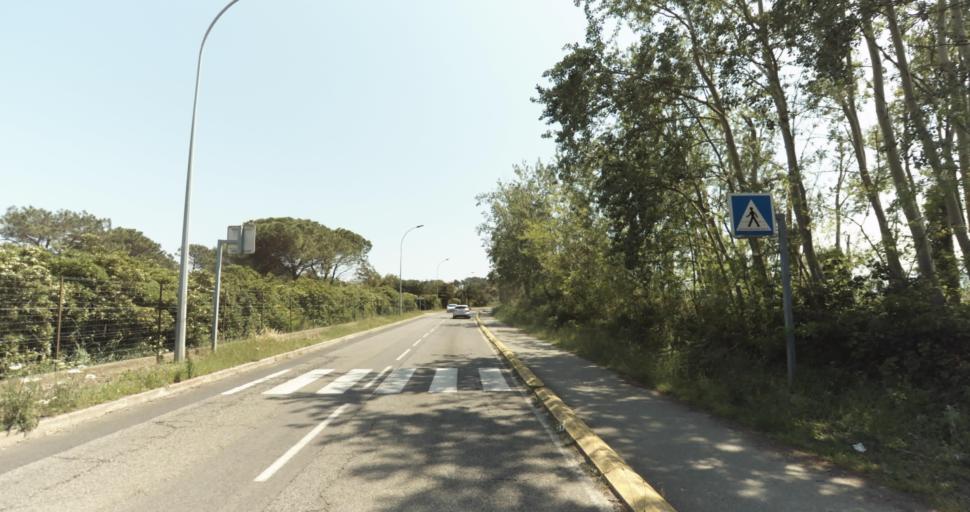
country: FR
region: Corsica
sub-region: Departement de la Haute-Corse
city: Biguglia
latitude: 42.6372
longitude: 9.4606
